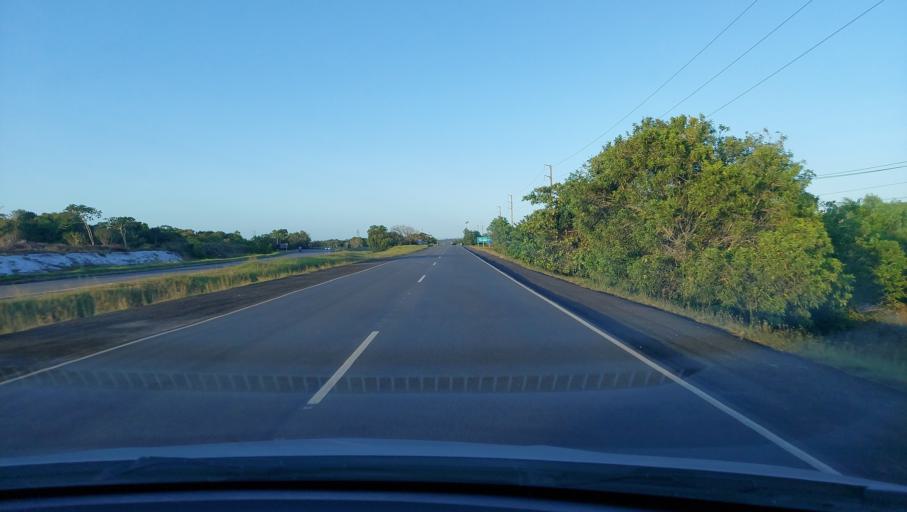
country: BR
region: Bahia
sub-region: Mata De Sao Joao
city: Mata de Sao Joao
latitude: -12.6198
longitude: -38.0580
